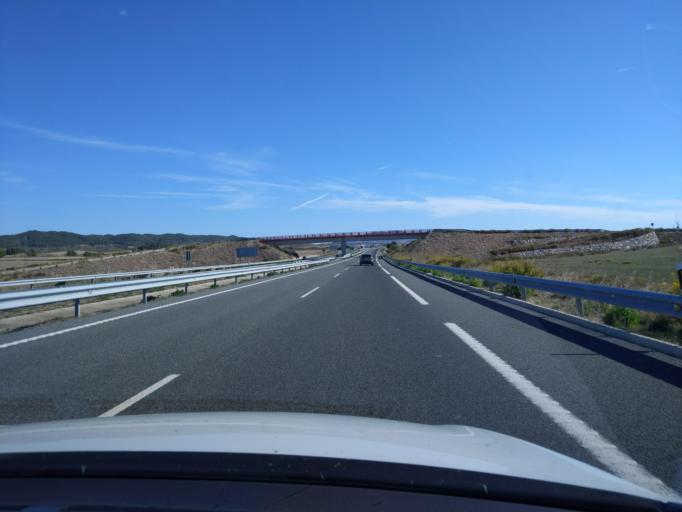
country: ES
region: Navarre
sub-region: Provincia de Navarra
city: Los Arcos
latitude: 42.5626
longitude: -2.1775
